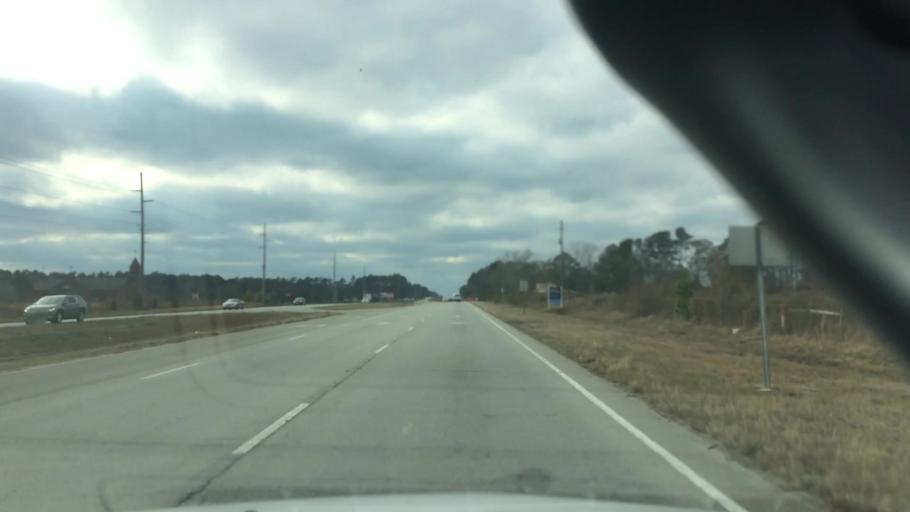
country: US
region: North Carolina
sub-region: Brunswick County
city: Shallotte
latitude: 33.9579
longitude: -78.4279
